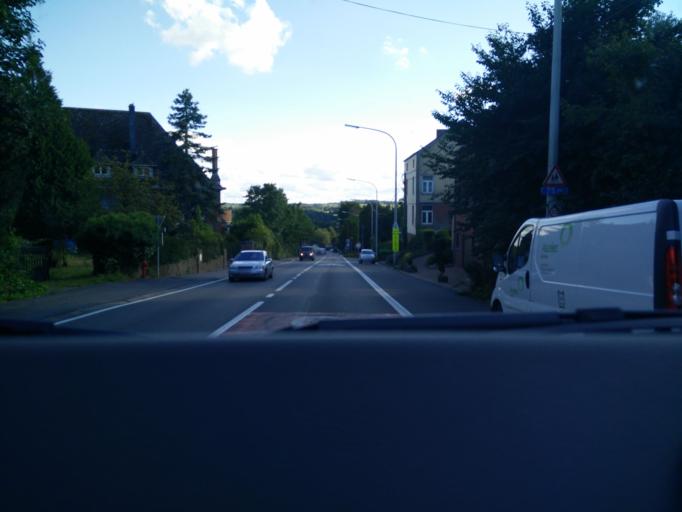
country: BE
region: Wallonia
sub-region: Province du Hainaut
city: Beaumont
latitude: 50.2342
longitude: 4.2382
